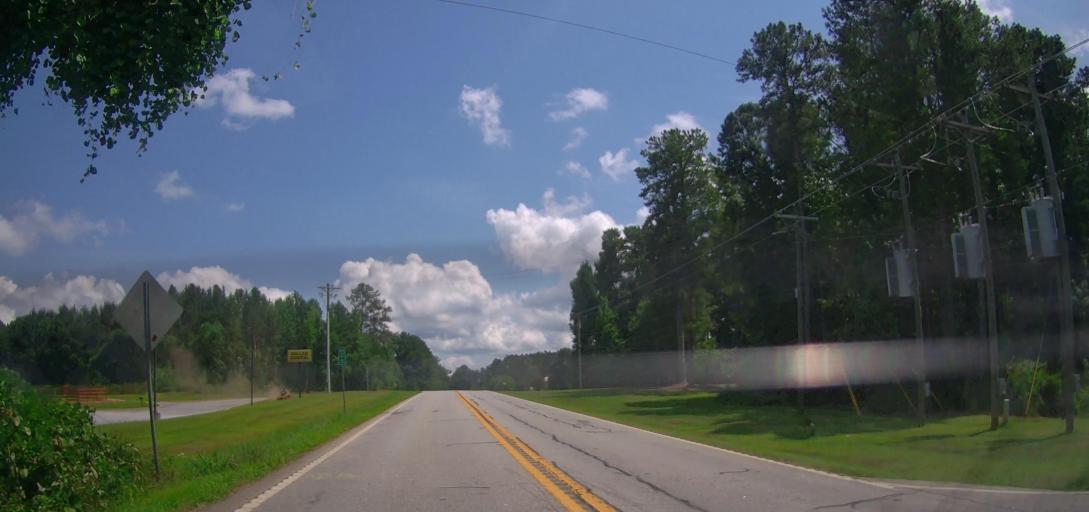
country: US
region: Georgia
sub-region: Carroll County
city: Bowdon
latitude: 33.4122
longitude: -85.2564
